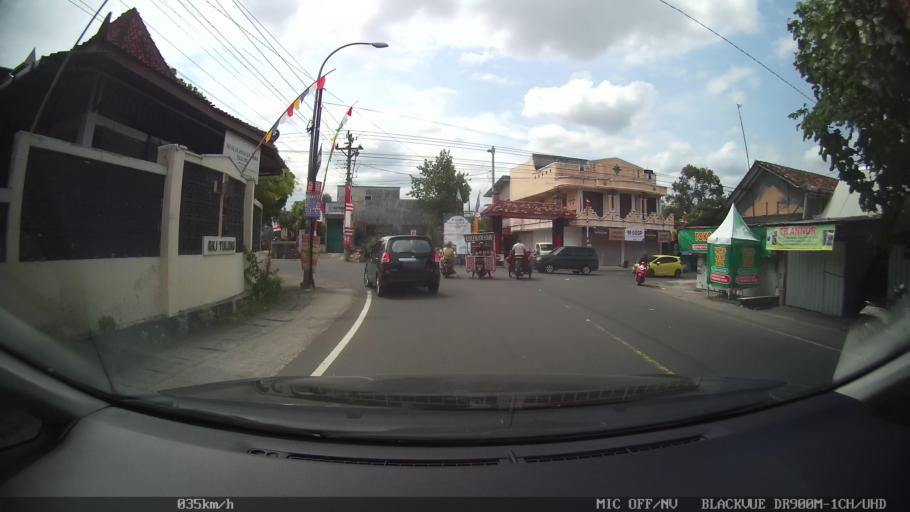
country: ID
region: Central Java
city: Candi Prambanan
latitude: -7.7367
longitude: 110.4822
